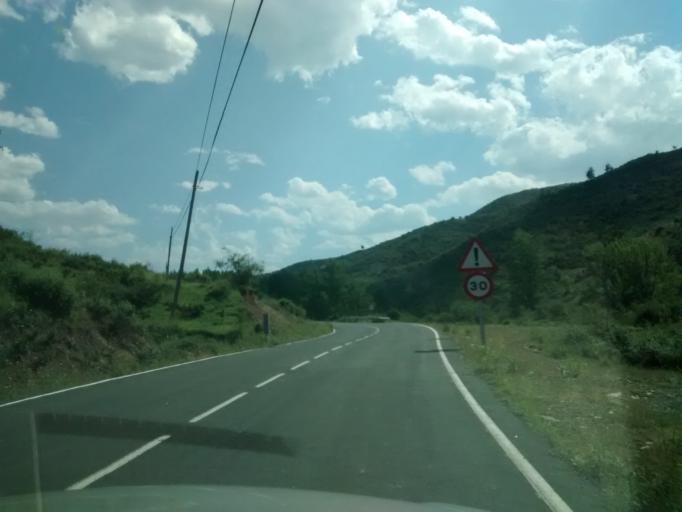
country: ES
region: La Rioja
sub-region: Provincia de La Rioja
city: Jalon de Cameros
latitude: 42.2072
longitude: -2.4789
